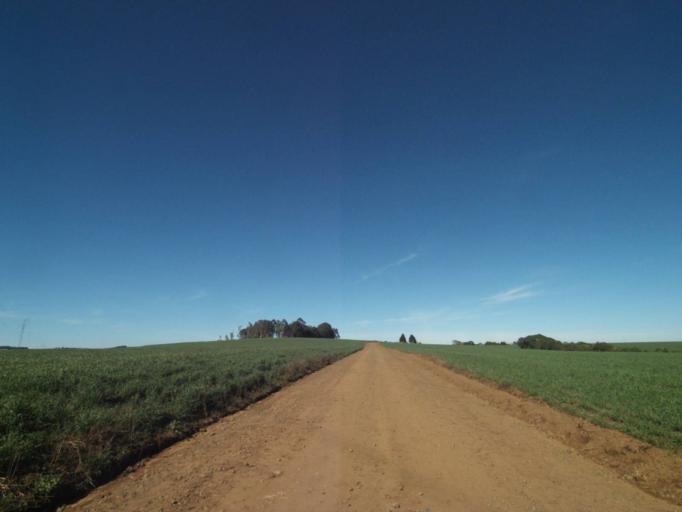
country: BR
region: Parana
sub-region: Tibagi
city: Tibagi
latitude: -24.5781
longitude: -50.2656
